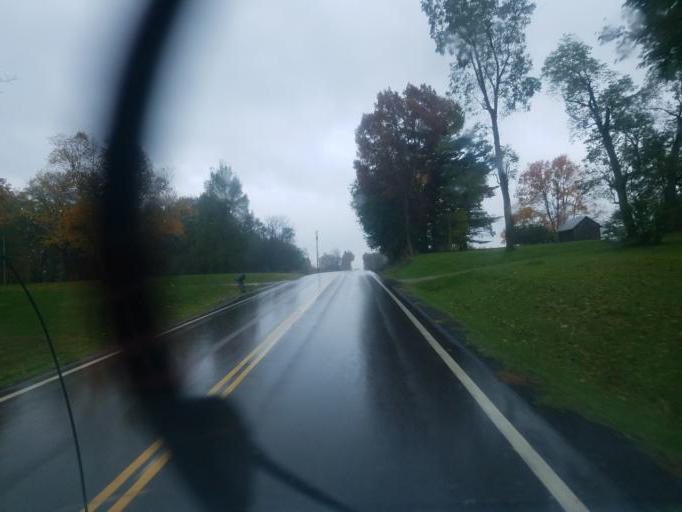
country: US
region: Ohio
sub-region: Knox County
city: Gambier
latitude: 40.3443
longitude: -82.4309
